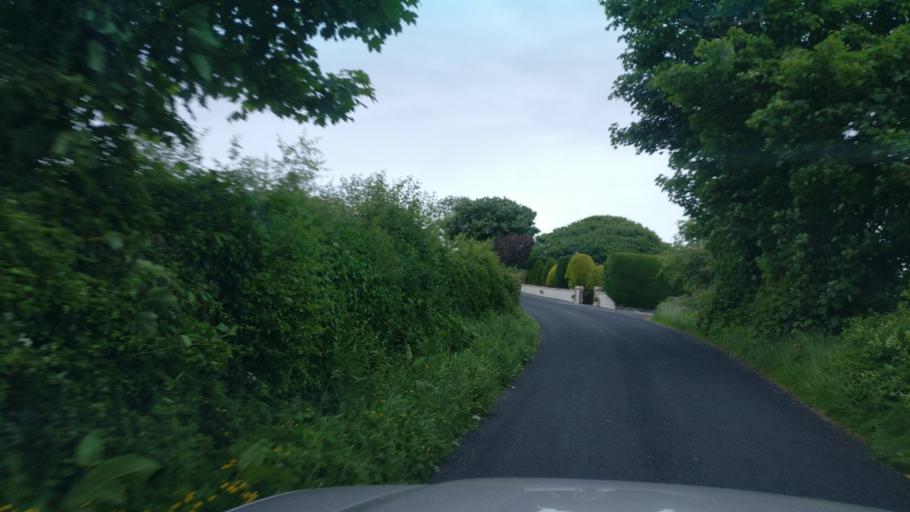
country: IE
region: Connaught
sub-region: County Galway
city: Loughrea
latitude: 53.1166
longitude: -8.4343
